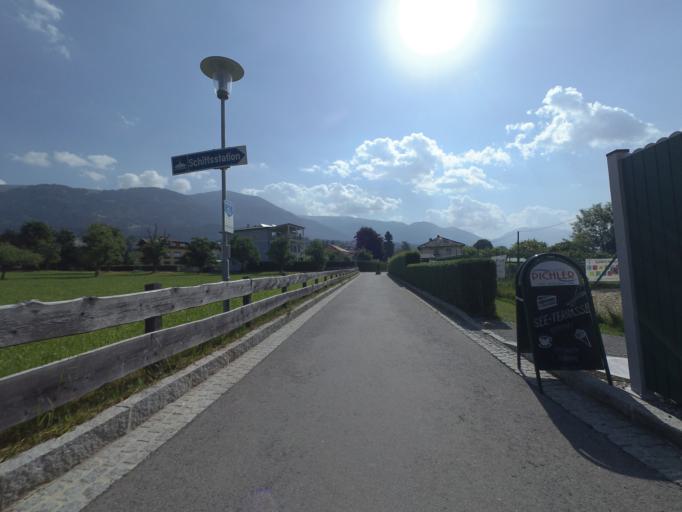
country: AT
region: Carinthia
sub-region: Politischer Bezirk Spittal an der Drau
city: Seeboden
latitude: 46.8153
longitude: 13.5230
